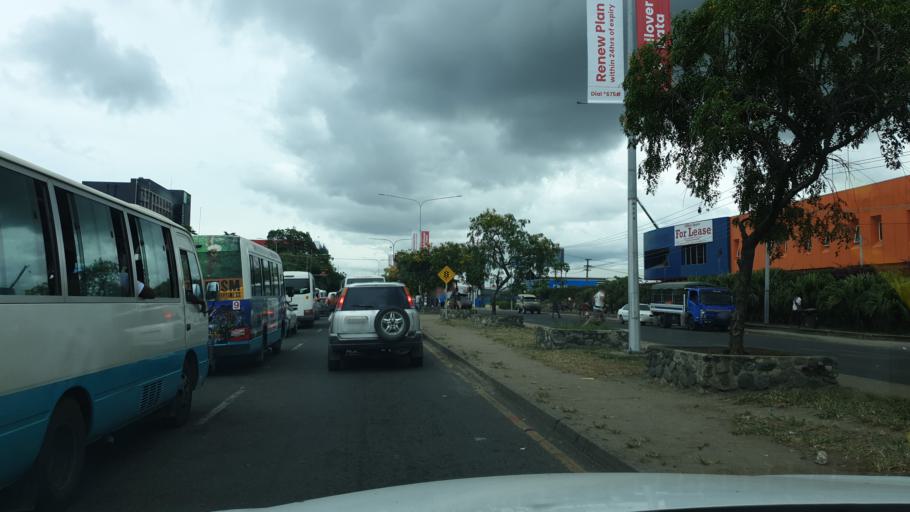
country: PG
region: National Capital
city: Port Moresby
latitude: -9.4473
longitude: 147.1839
